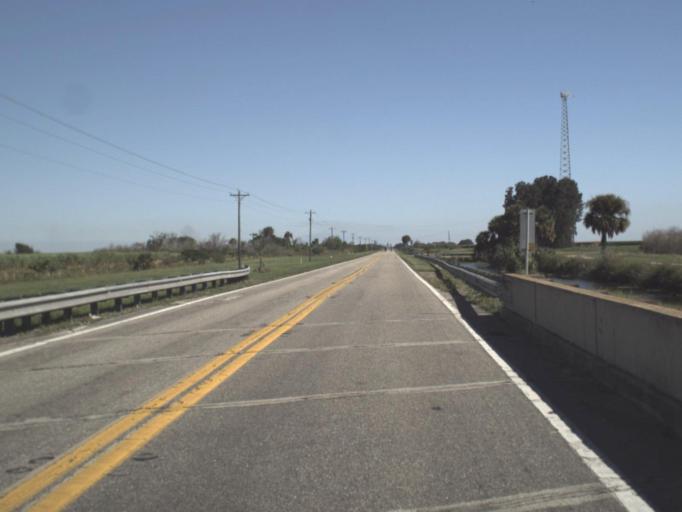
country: US
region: Florida
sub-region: Glades County
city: Moore Haven
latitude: 26.7674
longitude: -81.1719
